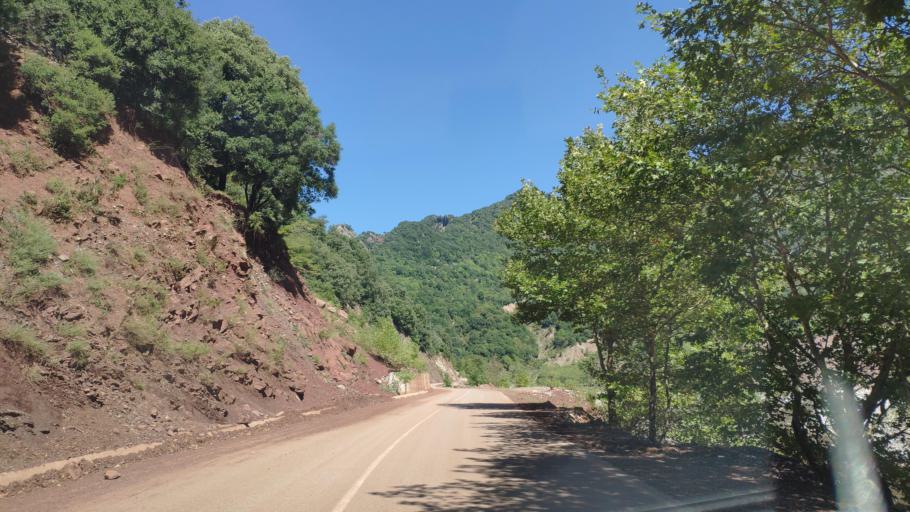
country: GR
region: Central Greece
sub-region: Nomos Evrytanias
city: Kerasochori
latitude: 39.0645
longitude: 21.6068
